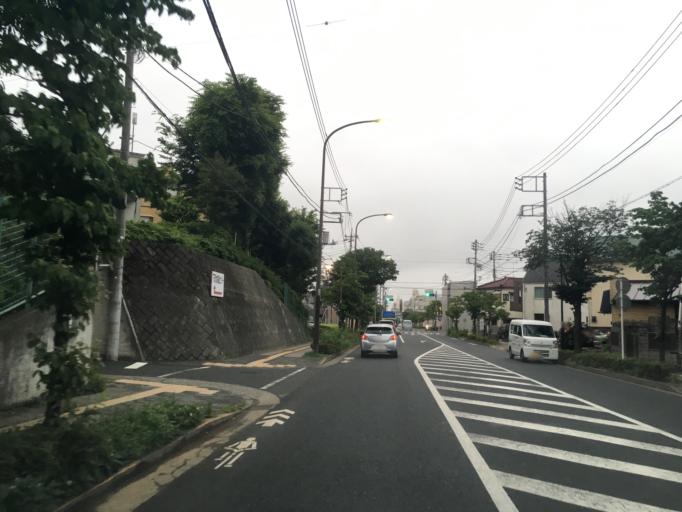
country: JP
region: Tokyo
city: Chofugaoka
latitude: 35.6475
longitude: 139.5342
